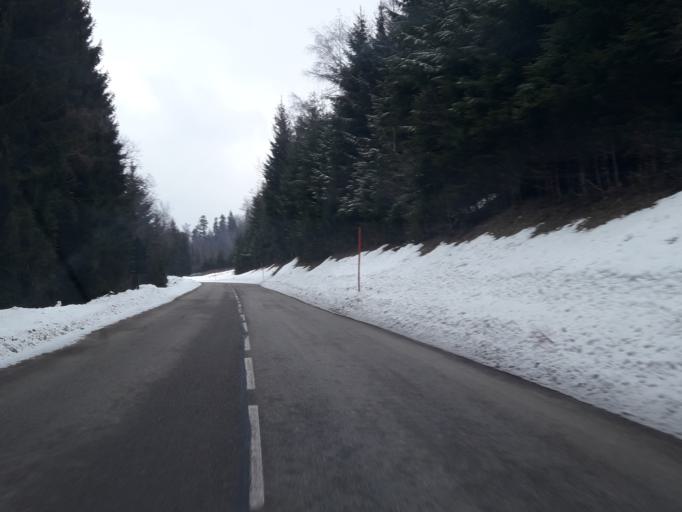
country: FR
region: Rhone-Alpes
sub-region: Departement de l'Isere
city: Theys
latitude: 45.2721
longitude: 6.0053
